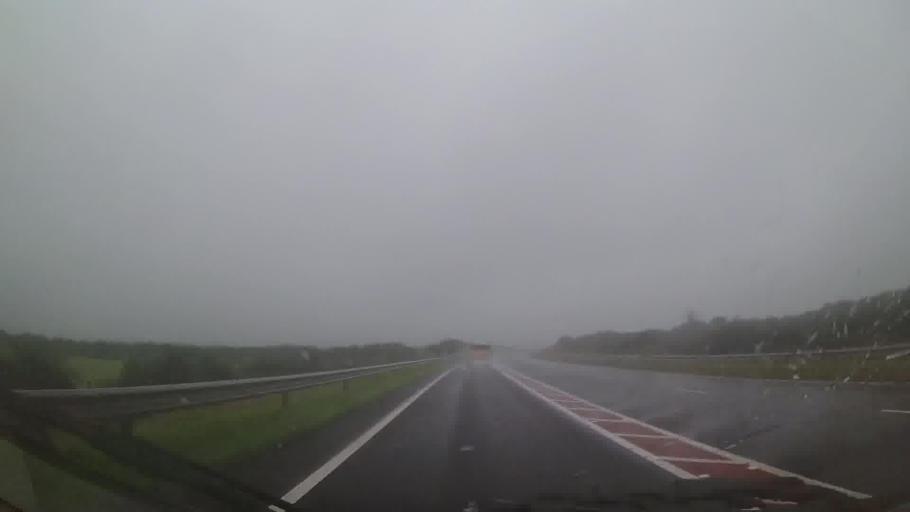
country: GB
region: Wales
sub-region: Carmarthenshire
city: Whitland
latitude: 51.7816
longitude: -4.6052
